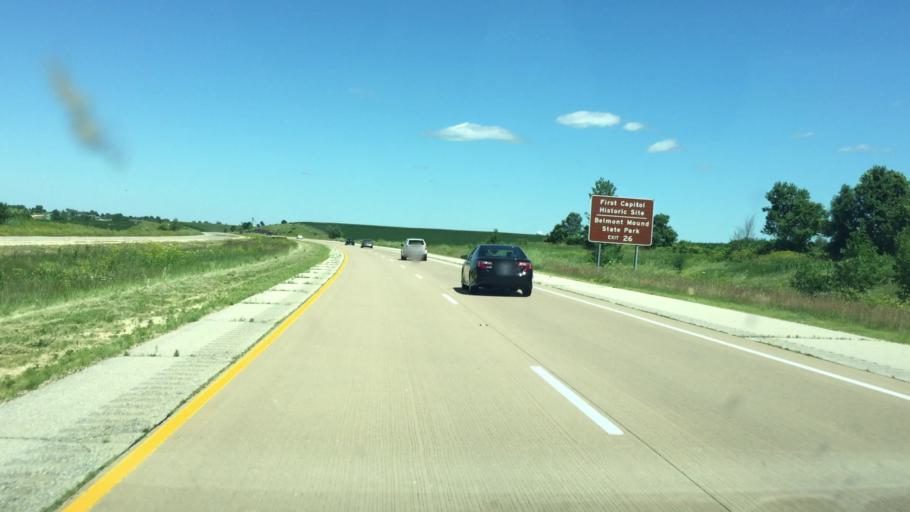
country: US
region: Wisconsin
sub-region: Grant County
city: Platteville
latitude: 42.7385
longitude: -90.3596
